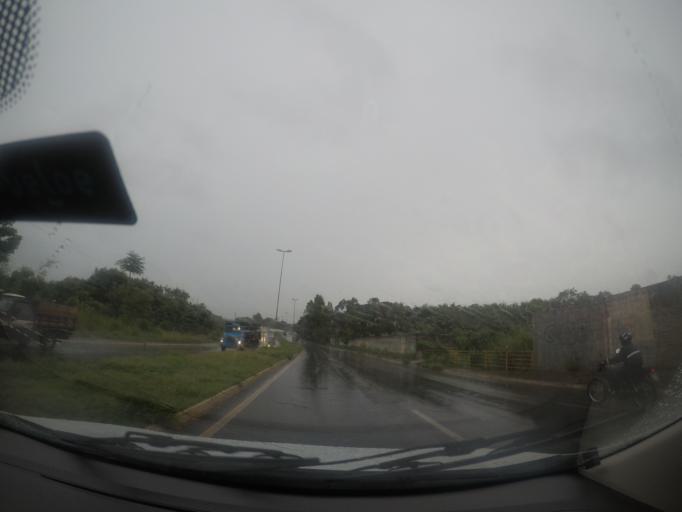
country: BR
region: Goias
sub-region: Goiania
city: Goiania
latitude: -16.6353
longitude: -49.3207
